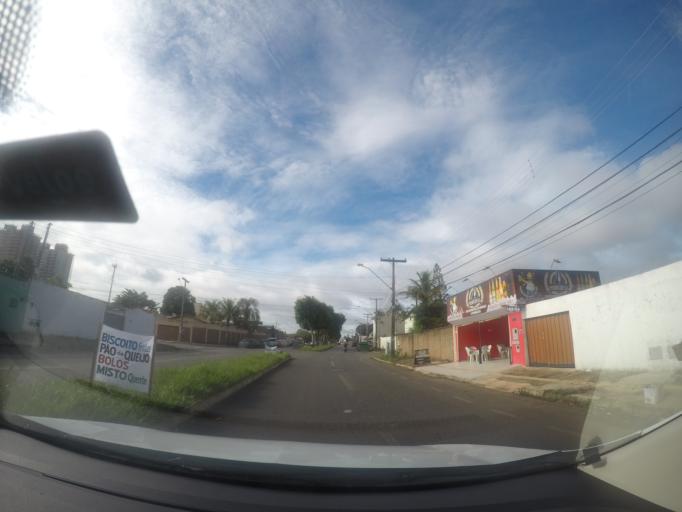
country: BR
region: Goias
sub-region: Goiania
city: Goiania
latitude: -16.6935
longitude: -49.3114
